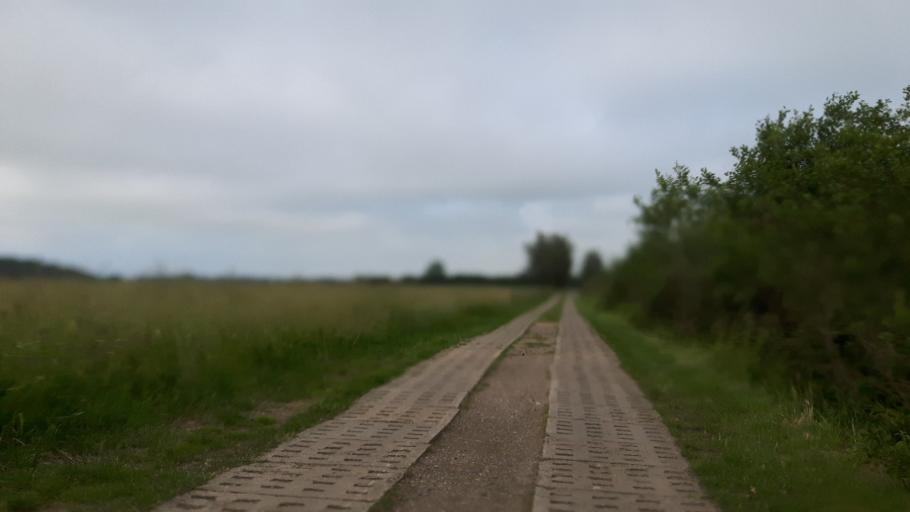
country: PL
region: West Pomeranian Voivodeship
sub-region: Powiat koszalinski
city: Sianow
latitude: 54.3081
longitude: 16.2875
